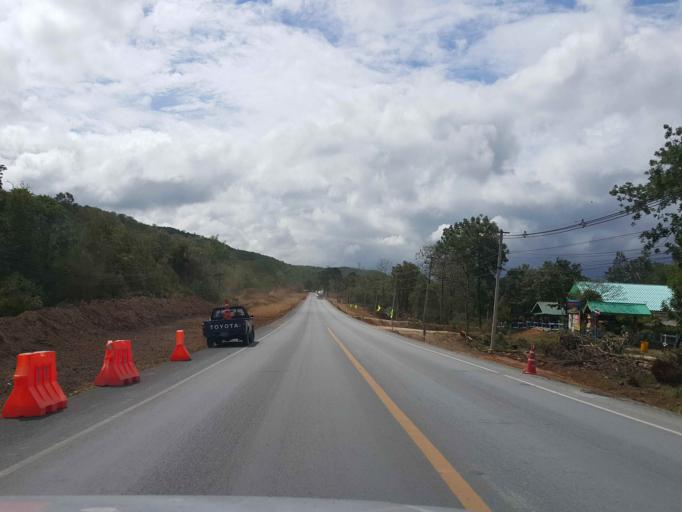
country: TH
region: Tak
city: Tak
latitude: 16.7977
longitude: 99.0080
